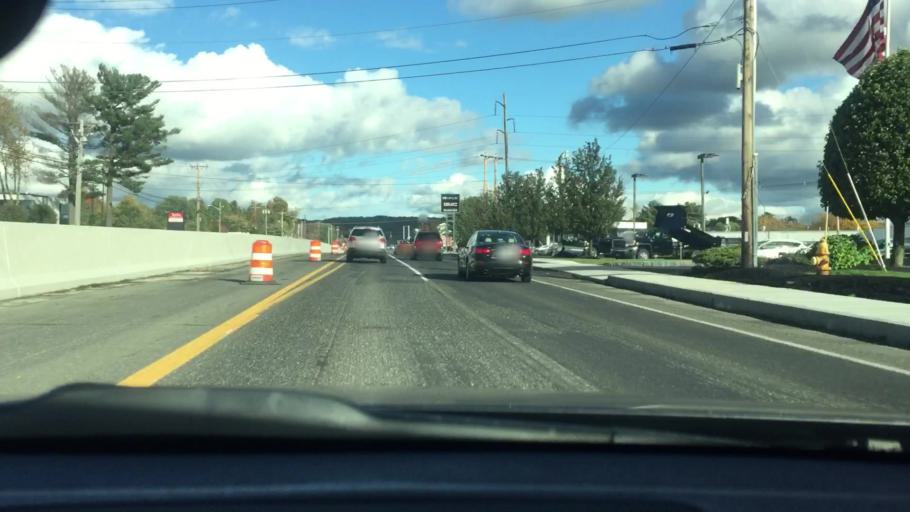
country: US
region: Massachusetts
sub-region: Worcester County
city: Westborough
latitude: 42.2848
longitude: -71.6133
